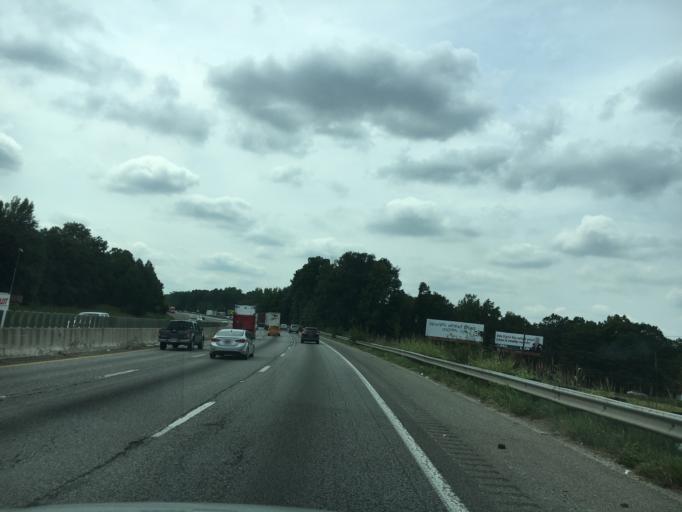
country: US
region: South Carolina
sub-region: Greenville County
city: Five Forks
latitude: 34.8527
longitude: -82.2763
